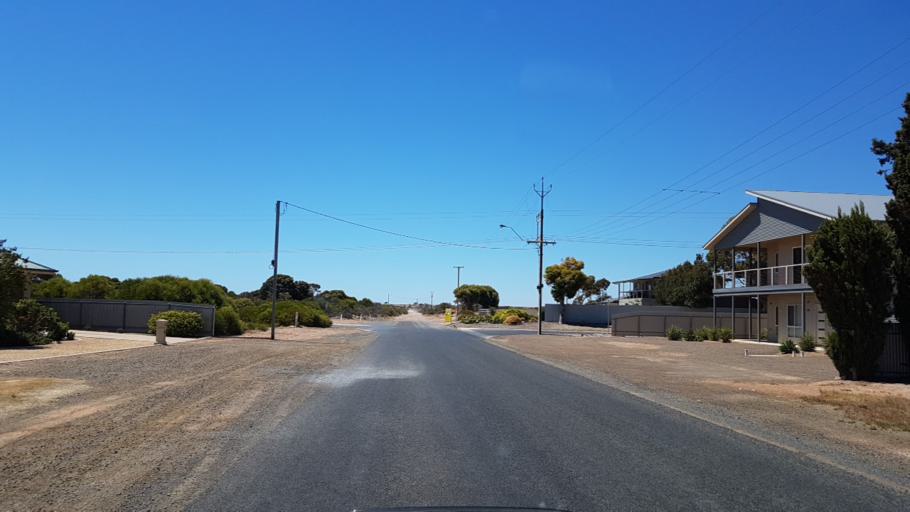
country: AU
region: South Australia
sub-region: Copper Coast
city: Wallaroo
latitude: -34.0487
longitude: 137.5685
